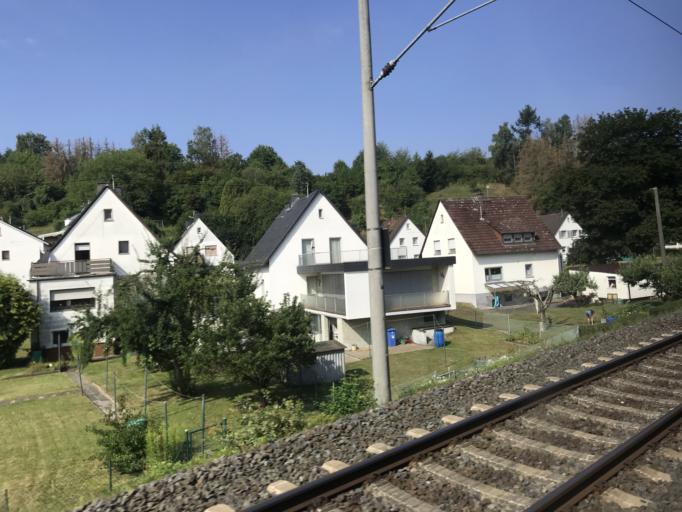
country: DE
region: Hesse
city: Bad Camberg
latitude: 50.3338
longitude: 8.2231
